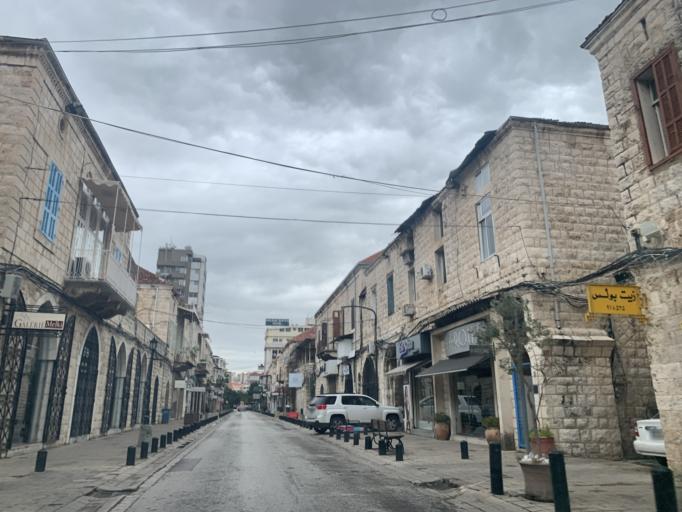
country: LB
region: Mont-Liban
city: Djounie
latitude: 33.9862
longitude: 35.6355
